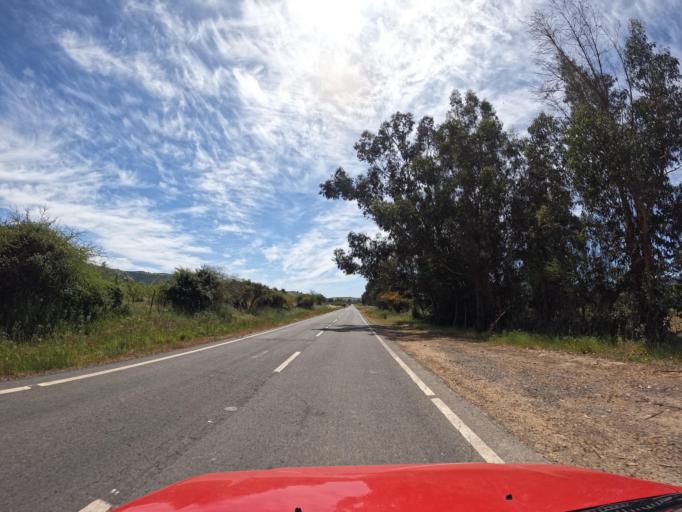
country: CL
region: Maule
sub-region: Provincia de Talca
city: Talca
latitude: -35.0365
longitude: -71.7574
